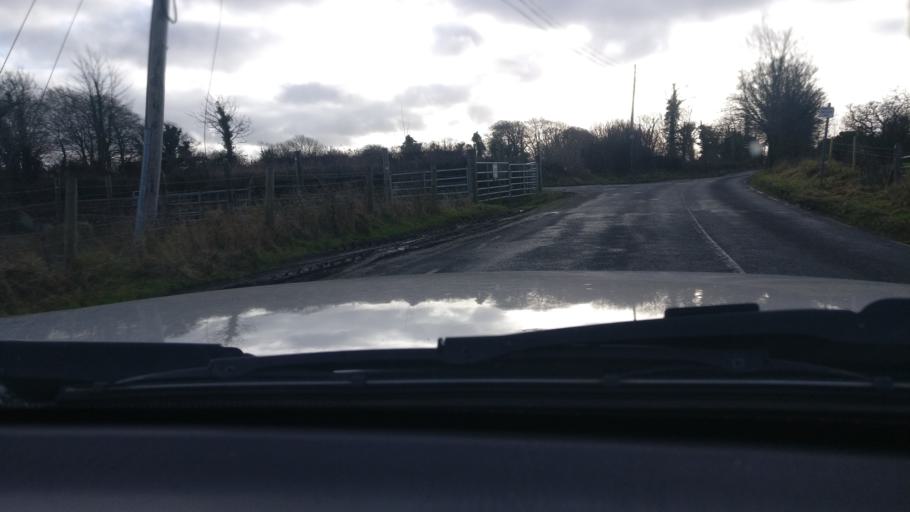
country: IE
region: Connaught
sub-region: County Galway
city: Ballinasloe
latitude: 53.2495
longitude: -8.2636
